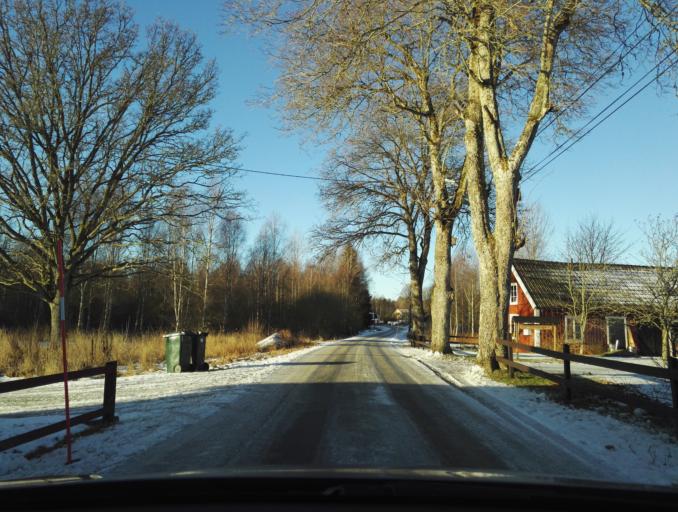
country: SE
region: Kronoberg
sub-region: Vaxjo Kommun
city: Gemla
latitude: 56.8509
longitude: 14.6295
